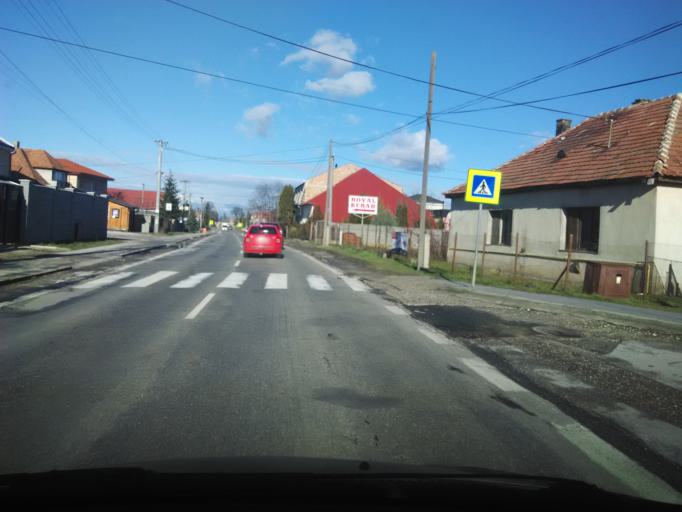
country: SK
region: Nitriansky
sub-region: Okres Nitra
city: Nitra
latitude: 48.2143
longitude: 18.1460
